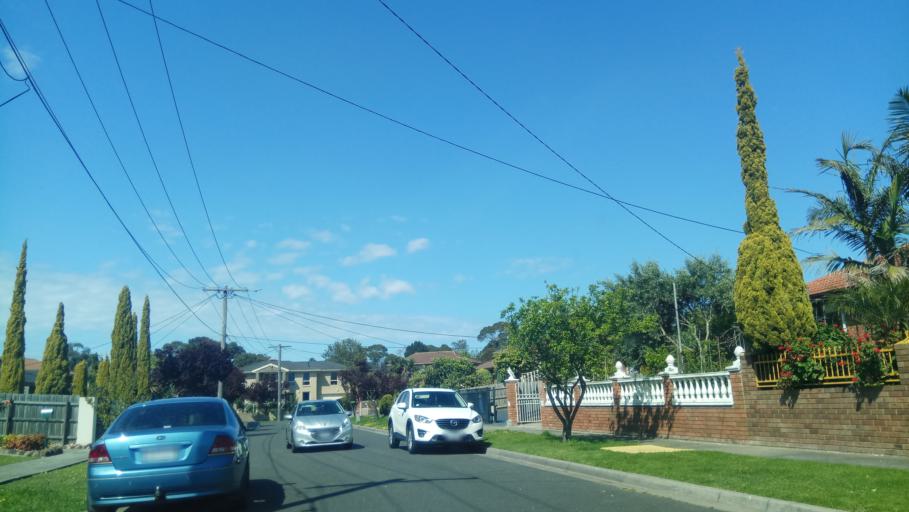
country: AU
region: Victoria
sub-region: Kingston
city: Clayton South
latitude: -37.9457
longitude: 145.1026
